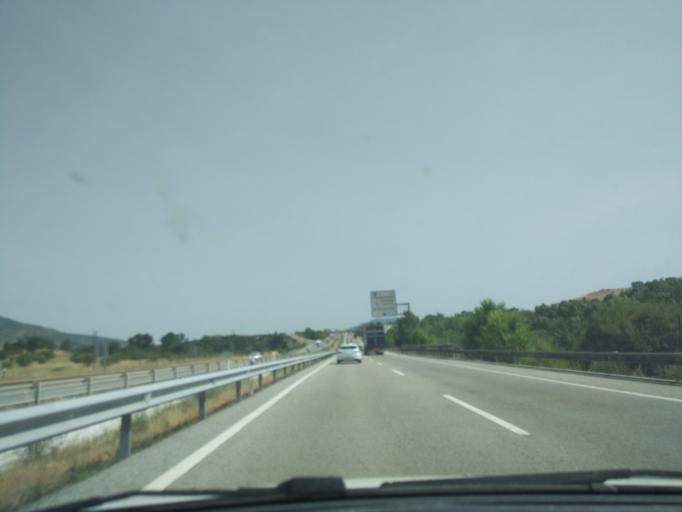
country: ES
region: Madrid
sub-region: Provincia de Madrid
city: Gascones
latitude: 41.0220
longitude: -3.6256
